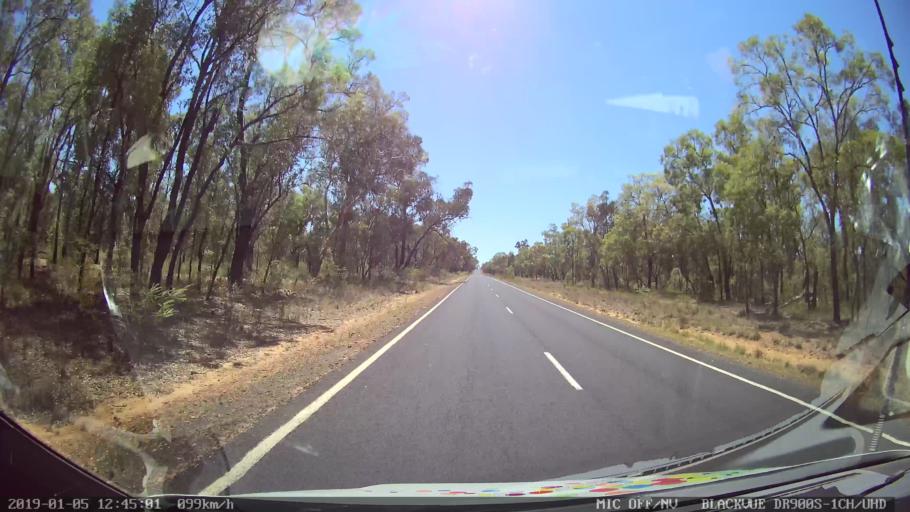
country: AU
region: New South Wales
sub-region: Warrumbungle Shire
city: Coonabarabran
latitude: -31.1319
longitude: 149.5447
